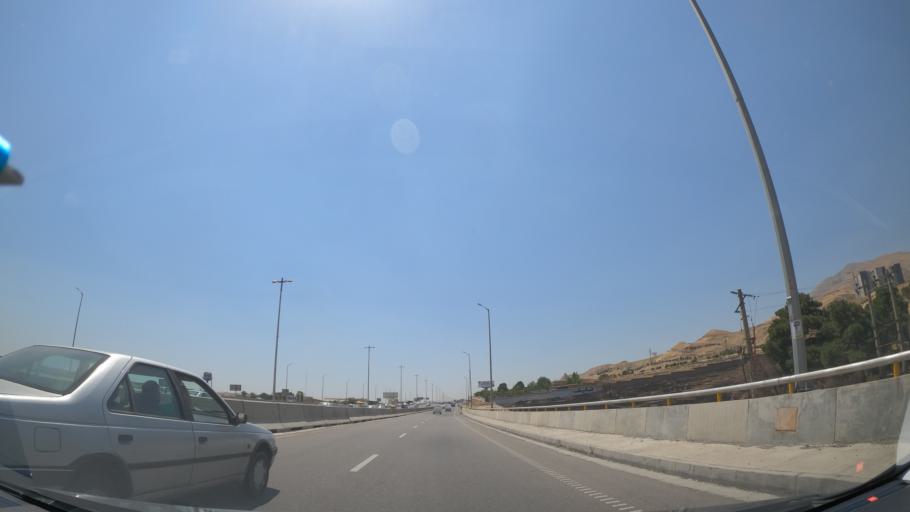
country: IR
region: Tehran
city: Shahr-e Qods
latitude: 35.7422
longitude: 51.1162
